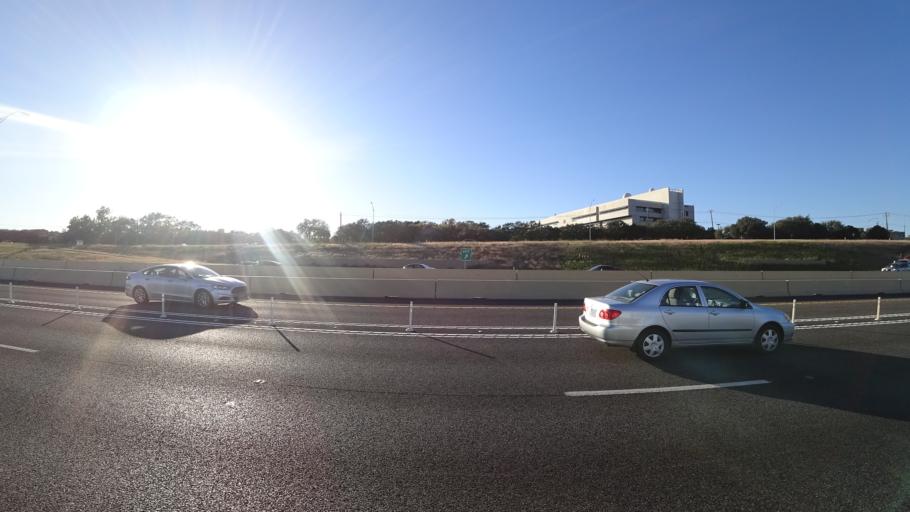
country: US
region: Texas
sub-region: Williamson County
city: Jollyville
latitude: 30.3941
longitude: -97.7330
